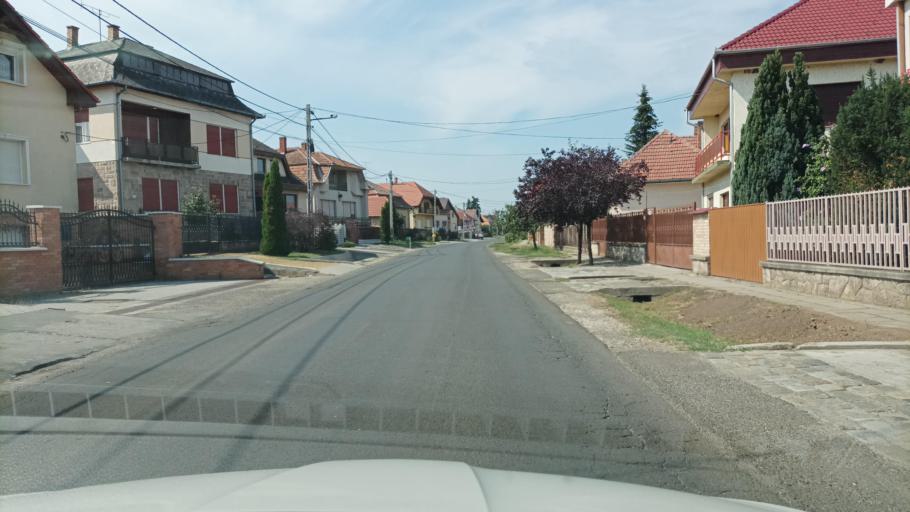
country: HU
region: Pest
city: Galgaheviz
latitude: 47.6226
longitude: 19.5448
